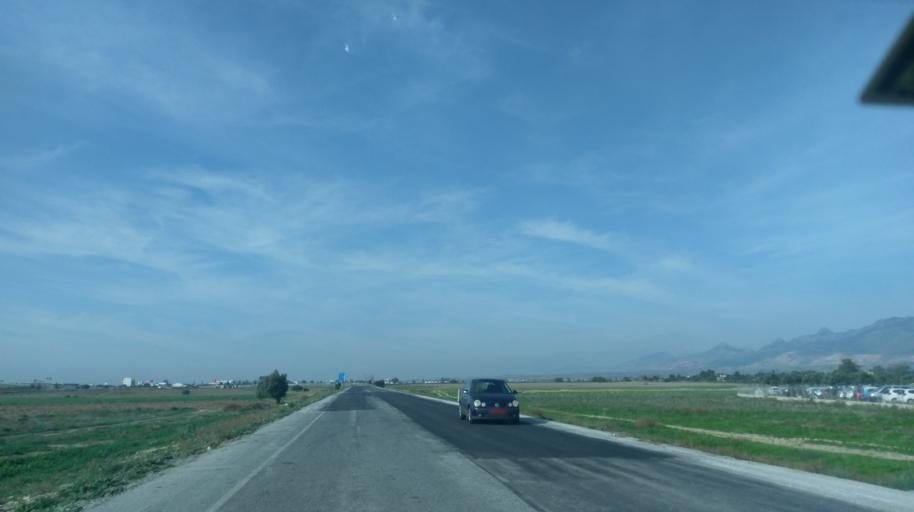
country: CY
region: Lefkosia
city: Geri
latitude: 35.2220
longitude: 33.5067
